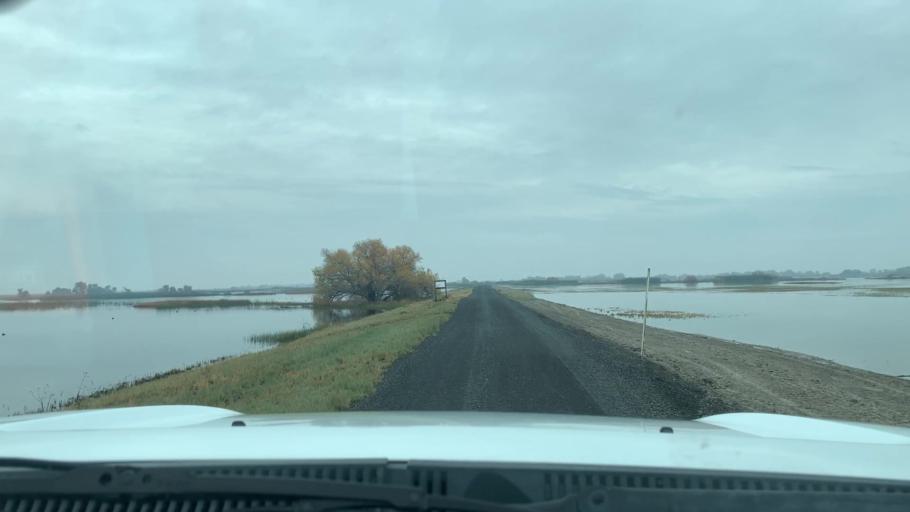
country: US
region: California
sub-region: Kern County
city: Lost Hills
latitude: 35.7393
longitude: -119.6079
